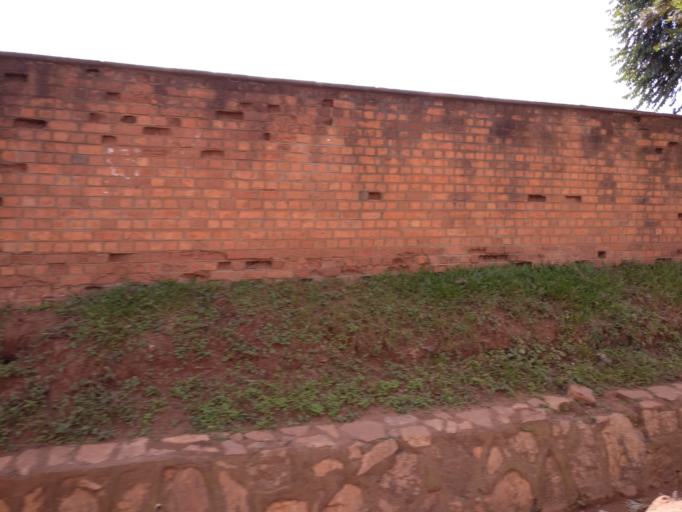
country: UG
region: Central Region
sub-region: Kampala District
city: Kampala
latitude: 0.2963
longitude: 32.5644
